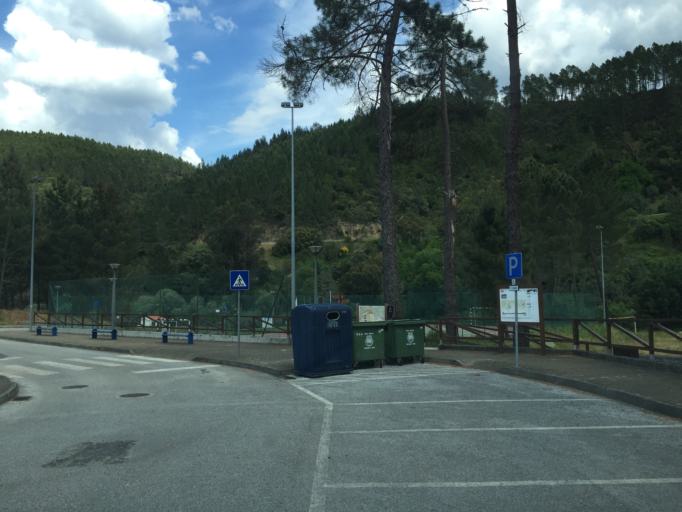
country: PT
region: Coimbra
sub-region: Pampilhosa da Serra
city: Pampilhosa da Serra
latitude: 40.0459
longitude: -7.8025
